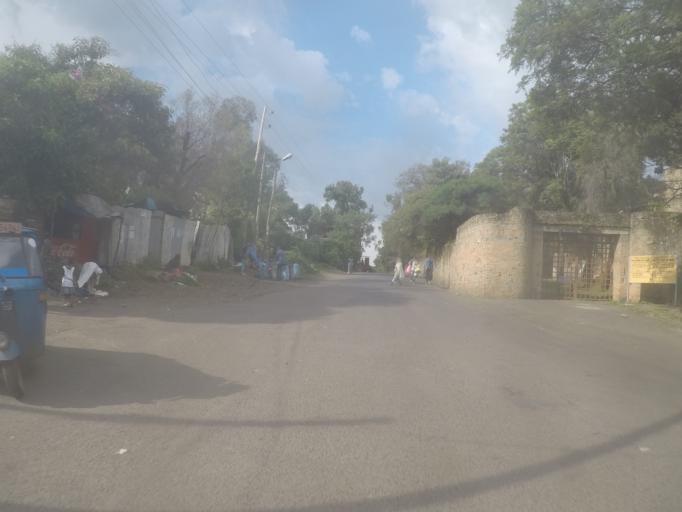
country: ET
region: Amhara
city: Gondar
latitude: 12.6126
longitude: 37.4710
